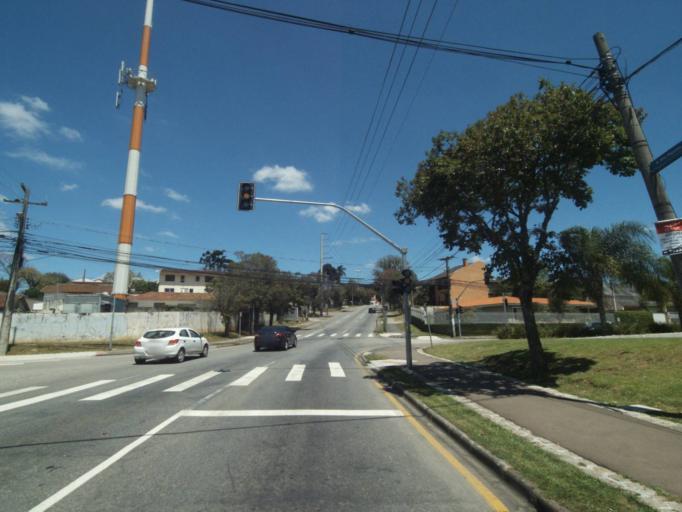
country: BR
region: Parana
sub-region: Curitiba
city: Curitiba
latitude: -25.3989
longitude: -49.2737
